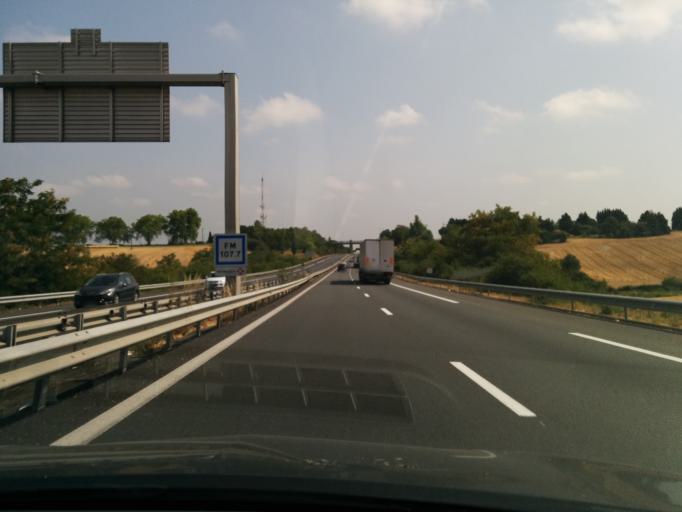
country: FR
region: Midi-Pyrenees
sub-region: Departement de la Haute-Garonne
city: Montastruc-la-Conseillere
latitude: 43.7272
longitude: 1.5728
